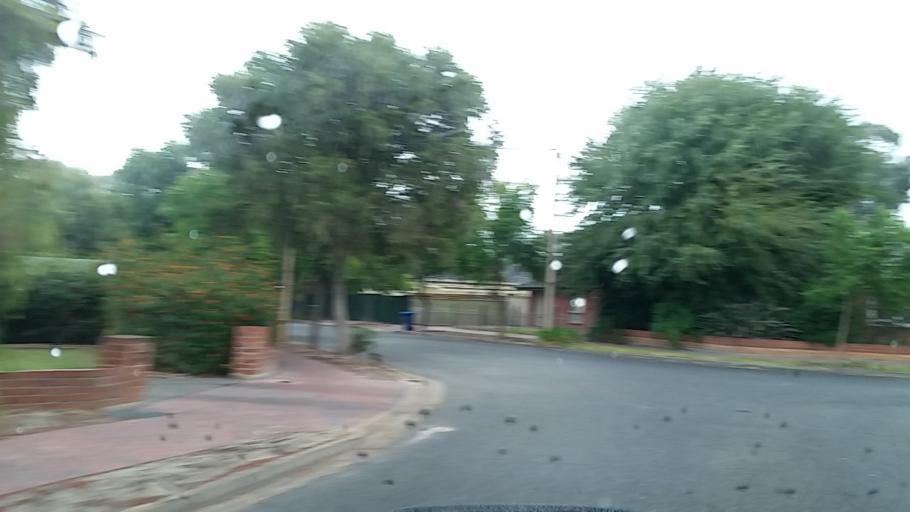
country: AU
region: South Australia
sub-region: Unley
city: Forestville
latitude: -34.9603
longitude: 138.5778
